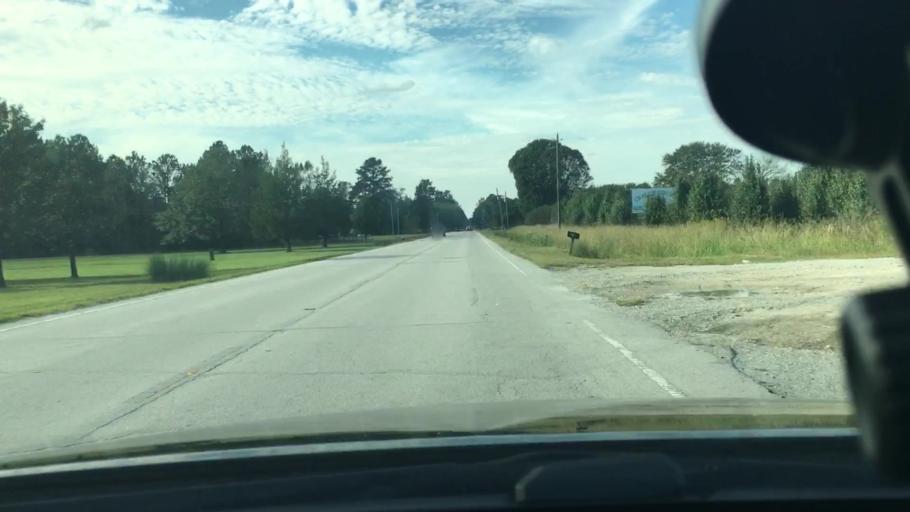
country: US
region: North Carolina
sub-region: Craven County
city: Vanceboro
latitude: 35.3852
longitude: -77.2266
